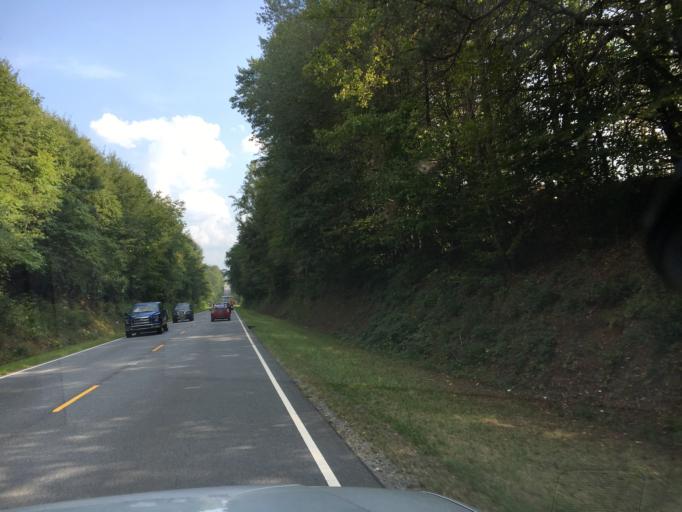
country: US
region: North Carolina
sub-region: Rutherford County
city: Rutherfordton
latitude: 35.3951
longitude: -81.9622
